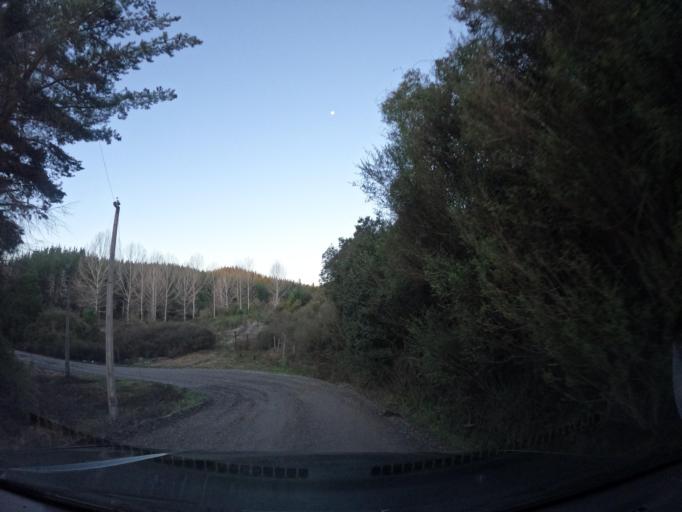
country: CL
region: Biobio
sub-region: Provincia de Concepcion
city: Chiguayante
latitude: -36.9942
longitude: -72.8274
